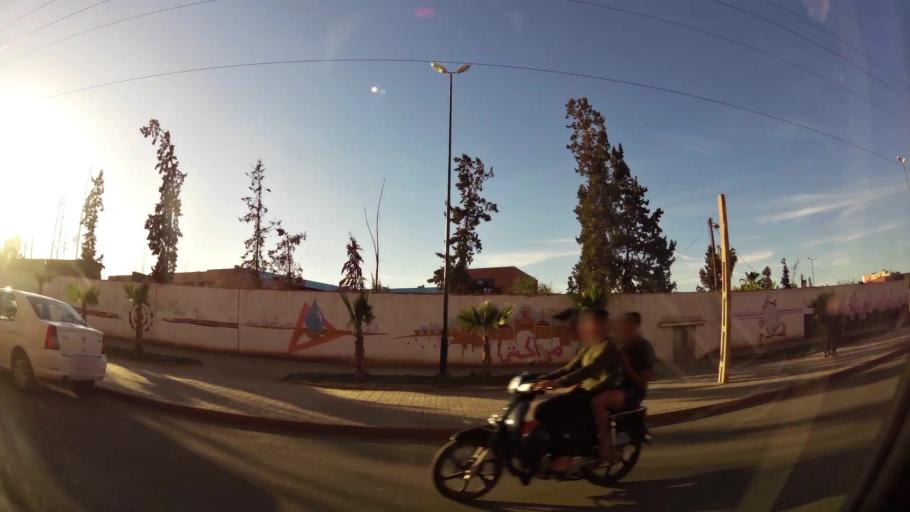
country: MA
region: Marrakech-Tensift-Al Haouz
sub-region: Marrakech
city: Marrakesh
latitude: 31.6195
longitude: -8.0522
